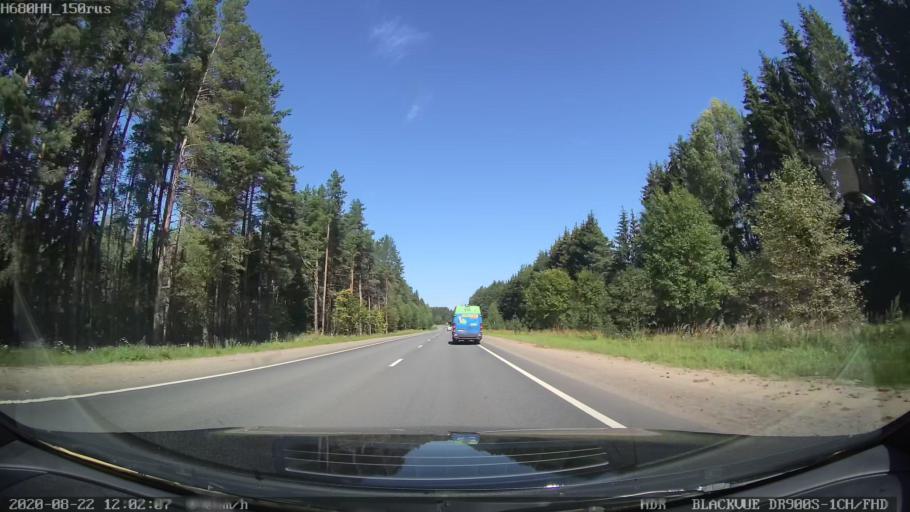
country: RU
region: Tverskaya
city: Rameshki
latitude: 57.2383
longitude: 36.1001
